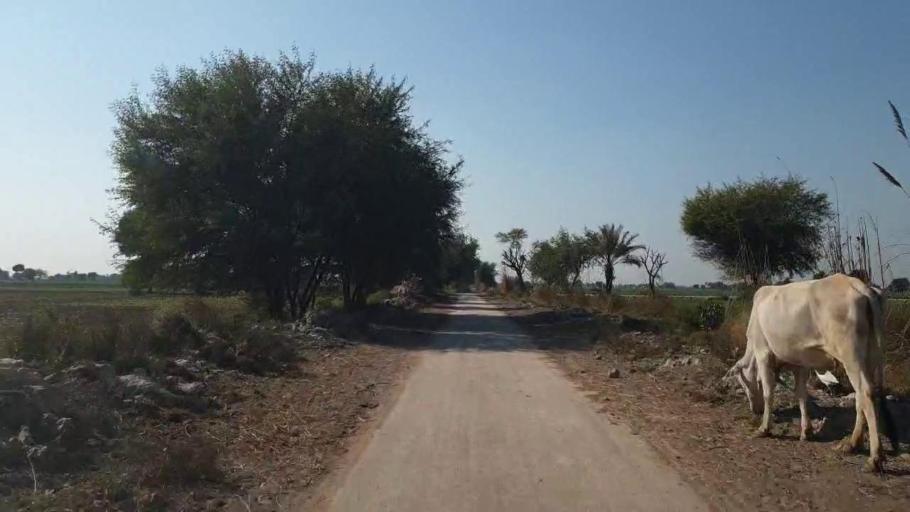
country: PK
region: Sindh
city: Shahdadpur
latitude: 25.9597
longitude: 68.6417
